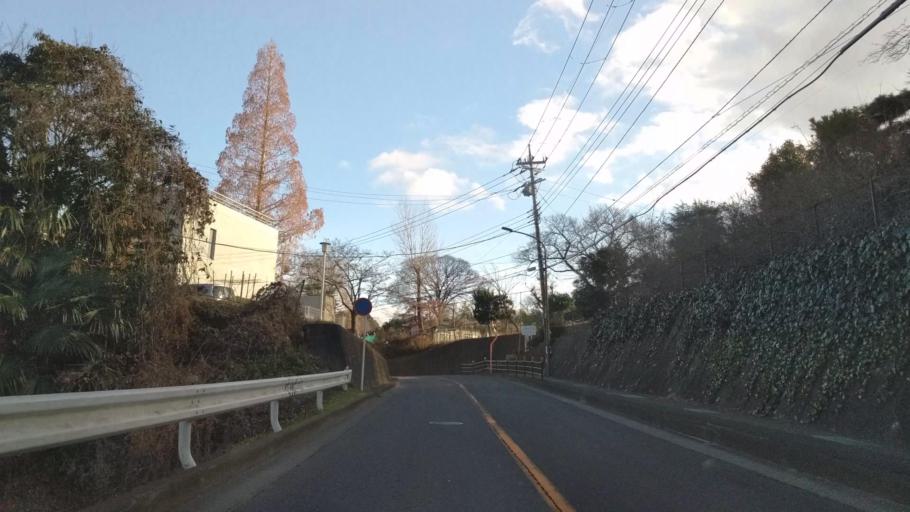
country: JP
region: Kanagawa
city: Ninomiya
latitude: 35.3464
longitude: 139.2696
